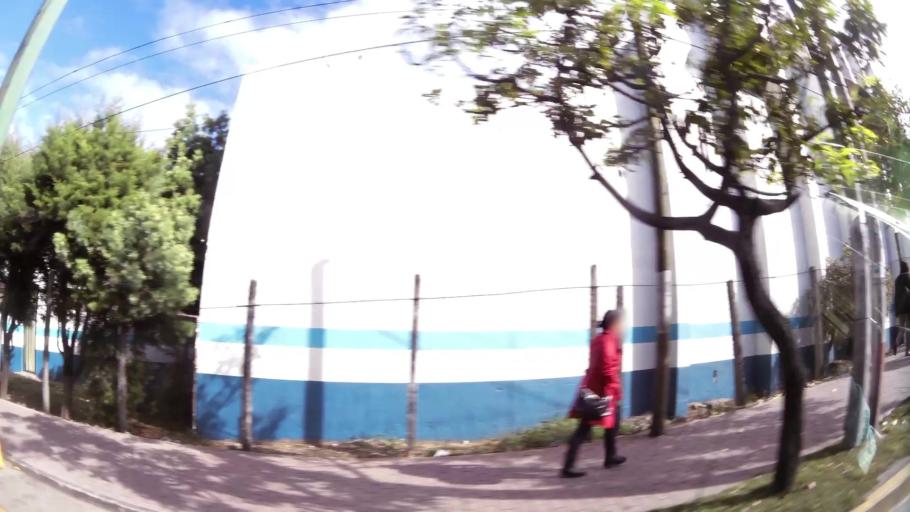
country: GT
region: Guatemala
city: Guatemala City
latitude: 14.6220
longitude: -90.5104
